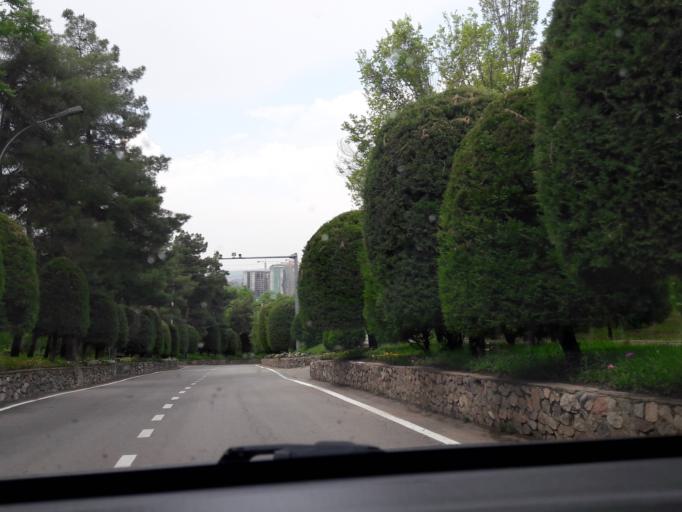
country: TJ
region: Dushanbe
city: Dushanbe
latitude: 38.5800
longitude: 68.8080
